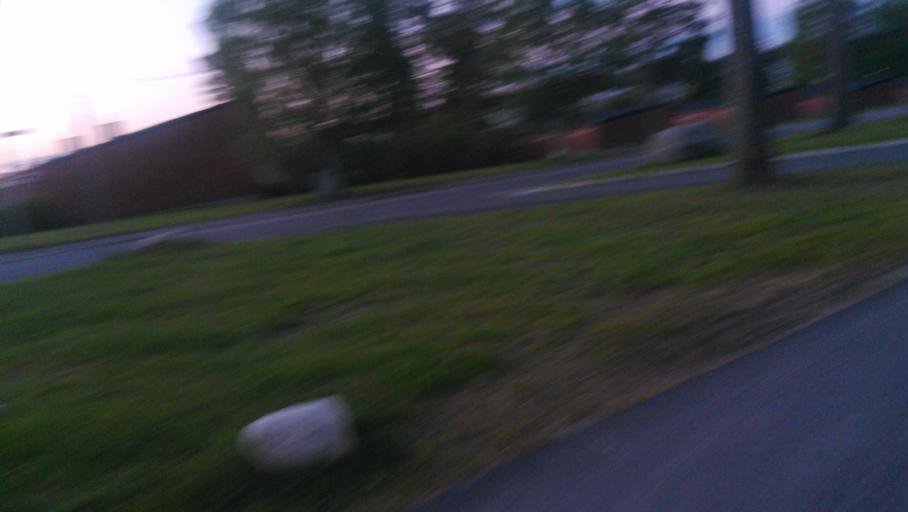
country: SE
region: Vaesterbotten
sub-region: Umea Kommun
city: Umea
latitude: 63.8280
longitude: 20.3042
